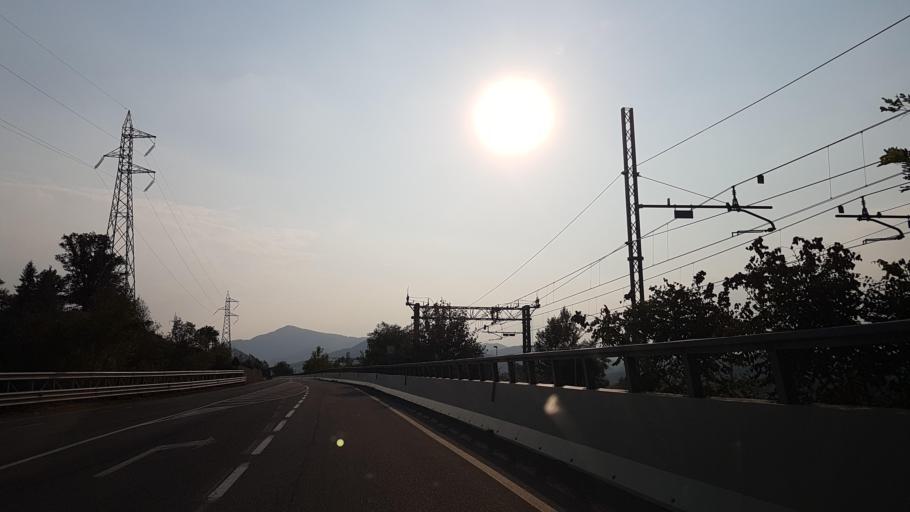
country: IT
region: Emilia-Romagna
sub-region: Provincia di Parma
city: Ramiola
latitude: 44.6754
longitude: 10.0836
